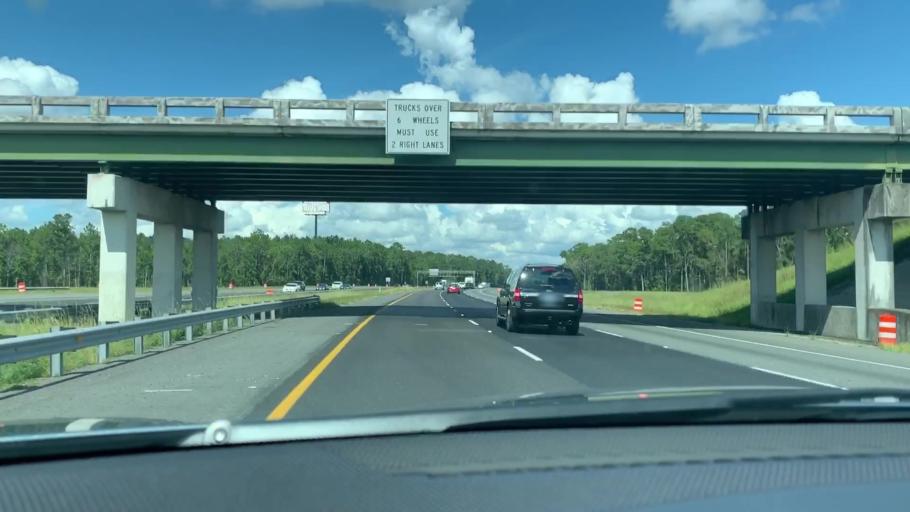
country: US
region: Georgia
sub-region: Camden County
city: Woodbine
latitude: 30.9458
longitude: -81.6863
